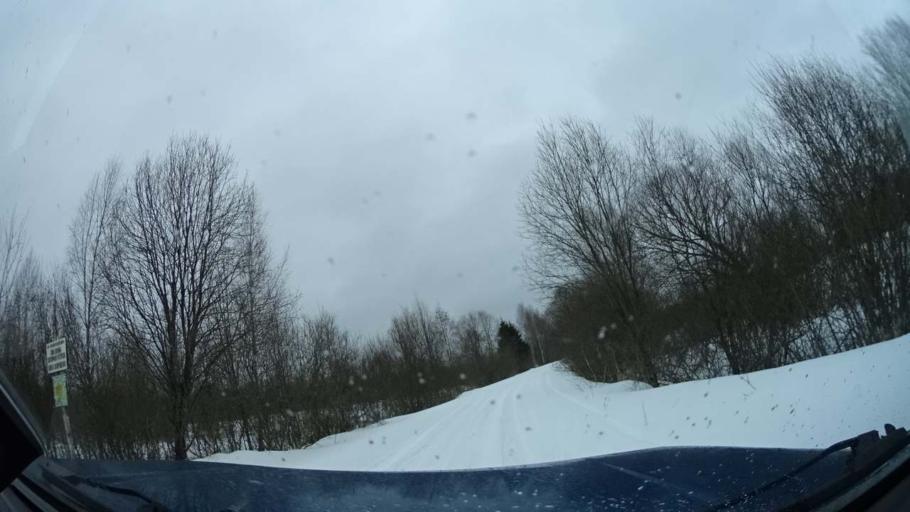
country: RU
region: Tverskaya
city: Gorodnya
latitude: 56.7883
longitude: 36.3622
